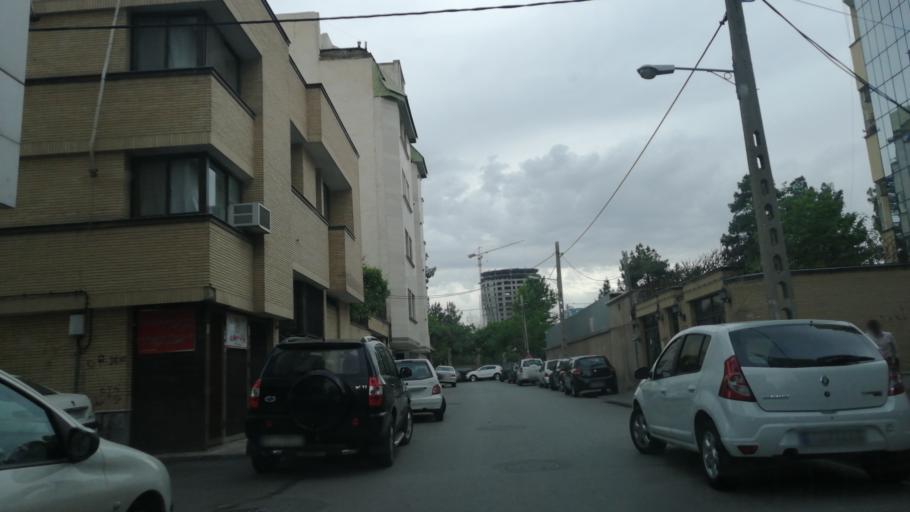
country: IR
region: Razavi Khorasan
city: Mashhad
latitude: 36.2886
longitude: 59.5822
